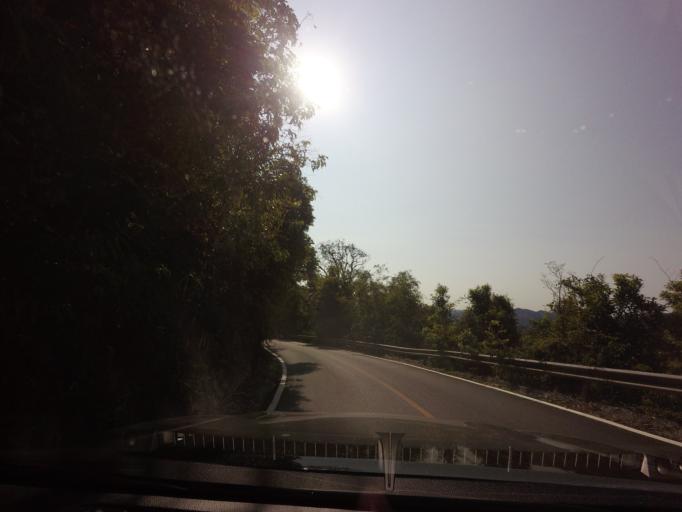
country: TH
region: Kanchanaburi
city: Thong Pha Phum
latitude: 14.6837
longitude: 98.4172
